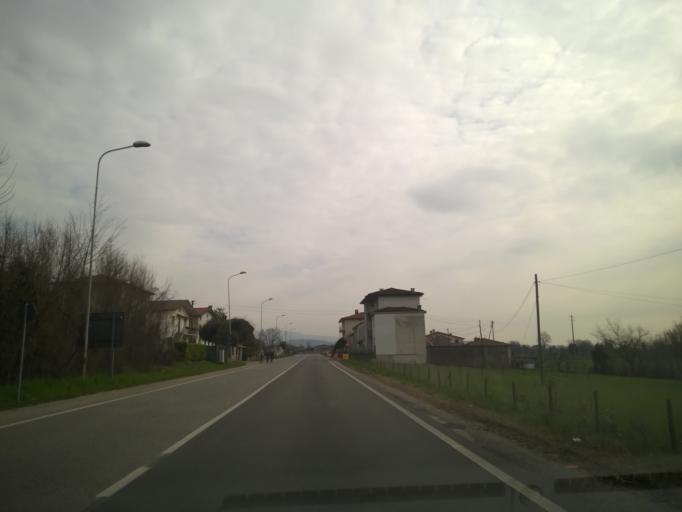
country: IT
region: Veneto
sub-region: Provincia di Vicenza
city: Santorso
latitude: 45.7373
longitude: 11.4057
